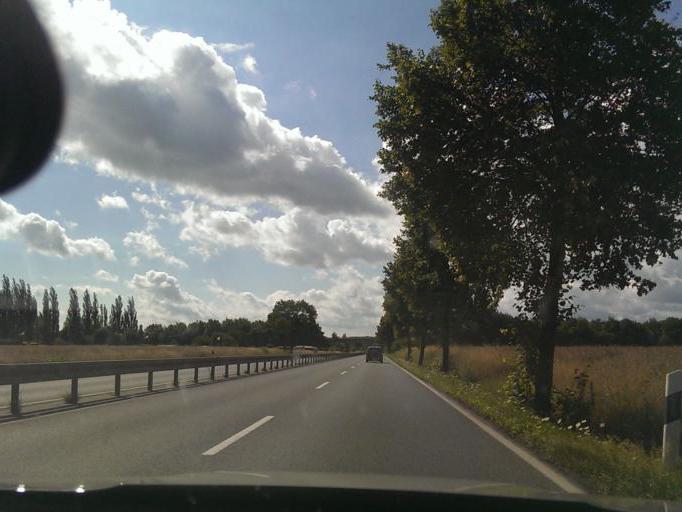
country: DE
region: Lower Saxony
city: Sarstedt
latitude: 52.2626
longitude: 9.8547
